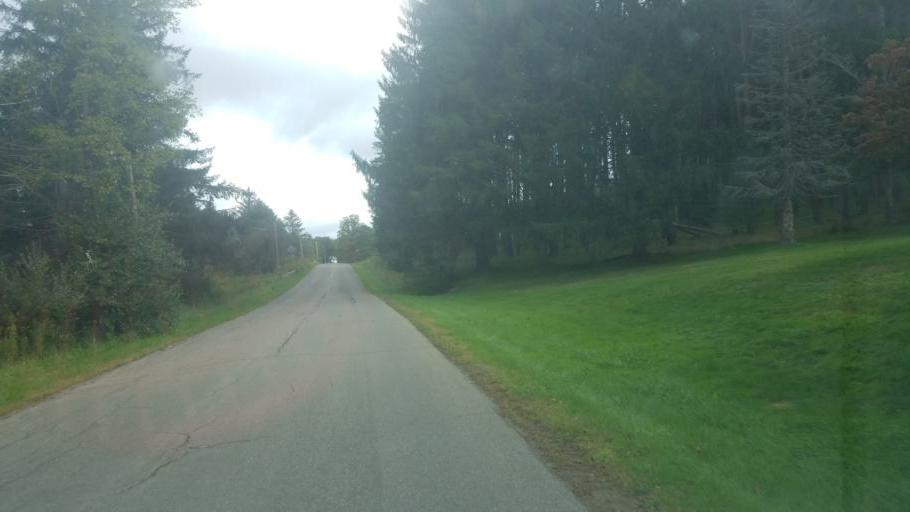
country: US
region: New York
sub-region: Cattaraugus County
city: Weston Mills
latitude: 42.1156
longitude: -78.3154
